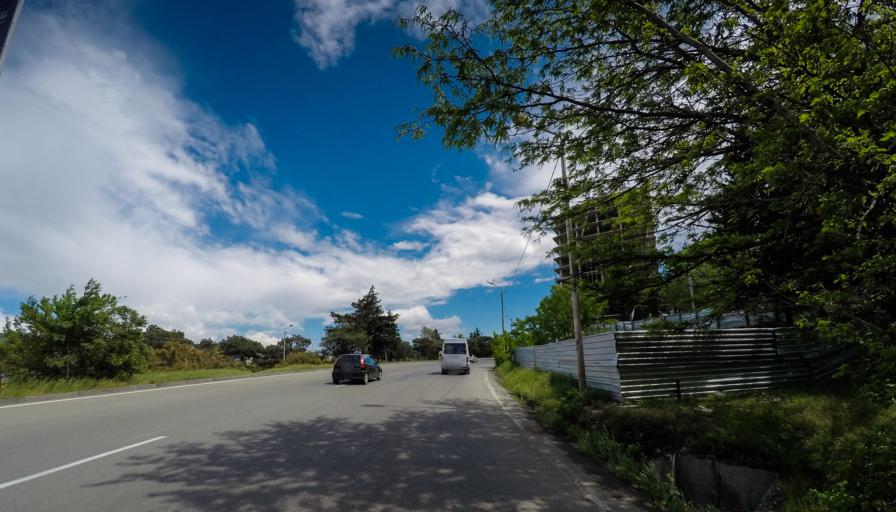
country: GE
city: Zahesi
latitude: 41.8230
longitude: 44.7684
